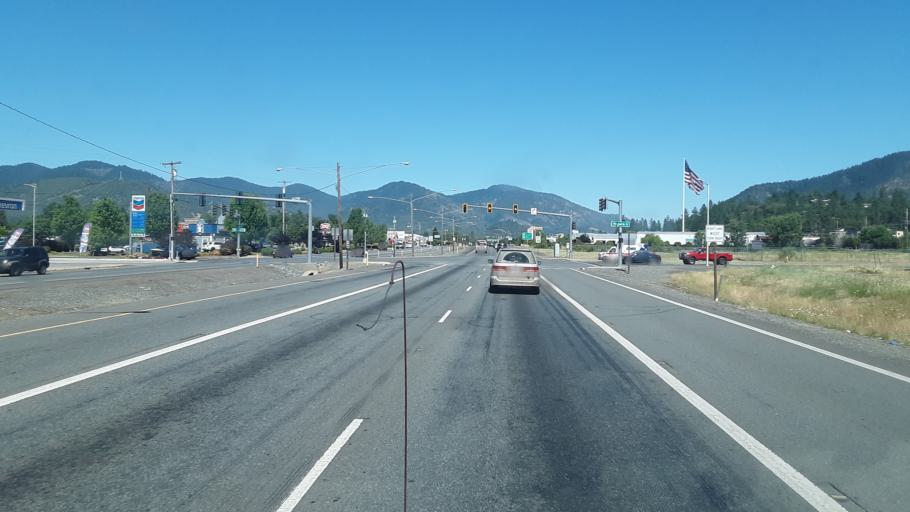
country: US
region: Oregon
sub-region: Josephine County
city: Grants Pass
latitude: 42.4232
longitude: -123.3410
